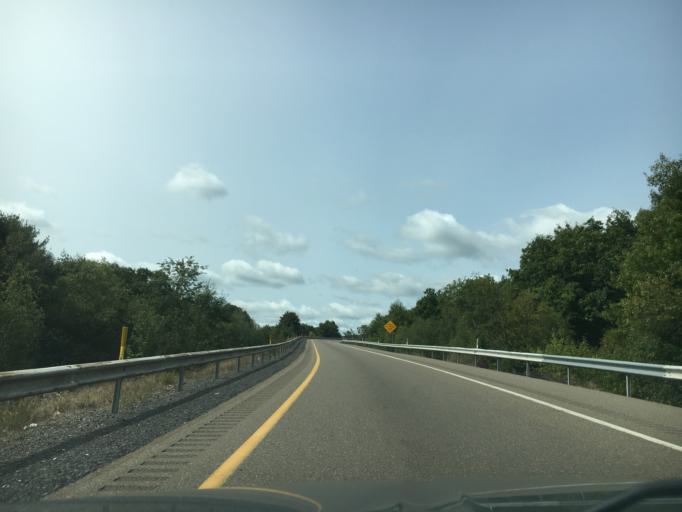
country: US
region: Pennsylvania
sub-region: Schuylkill County
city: McAdoo
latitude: 40.8849
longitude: -76.0126
